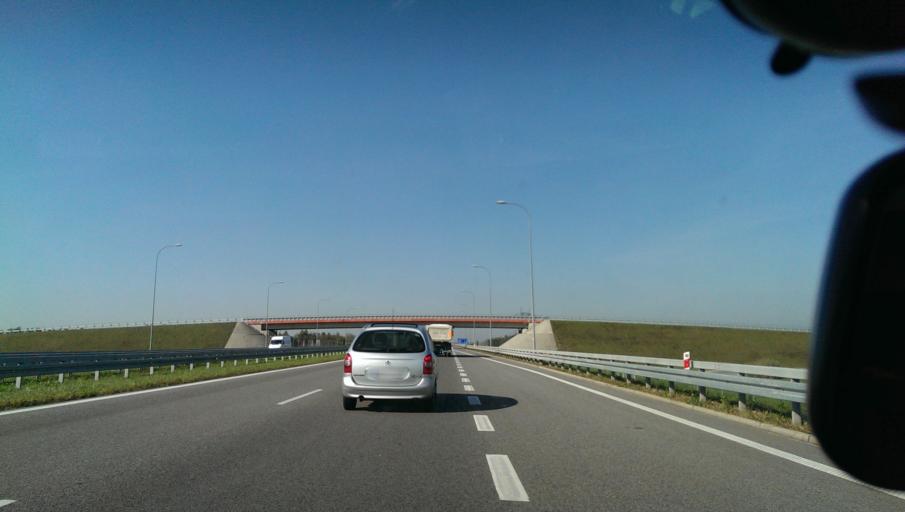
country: PL
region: Subcarpathian Voivodeship
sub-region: Powiat rzeszowski
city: Swilcza
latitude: 50.1058
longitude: 21.9140
